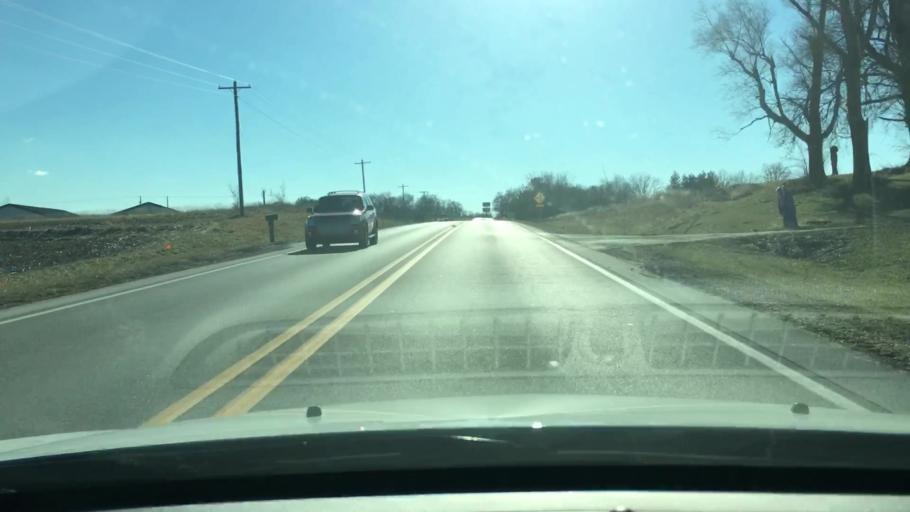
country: US
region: Illinois
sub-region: Pike County
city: Pittsfield
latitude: 39.6370
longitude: -90.7877
